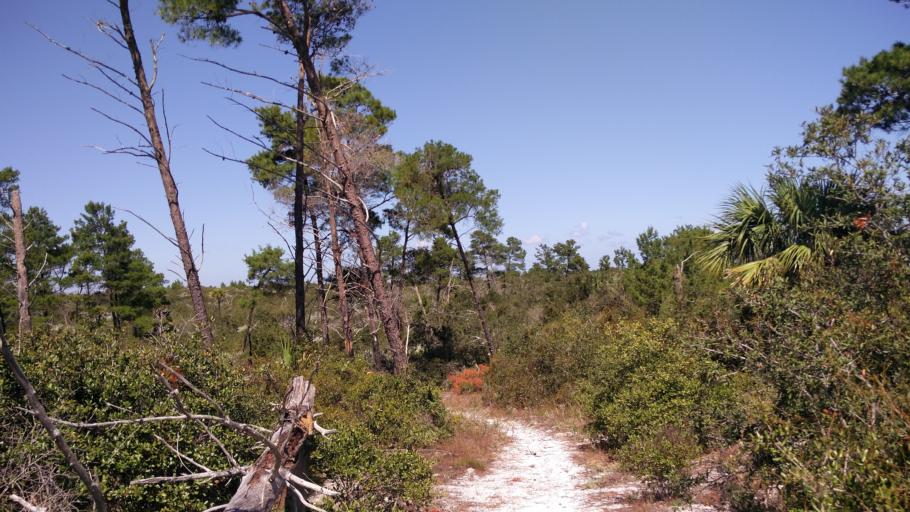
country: US
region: Florida
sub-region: Martin County
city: Hobe Sound
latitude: 27.0273
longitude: -80.1182
